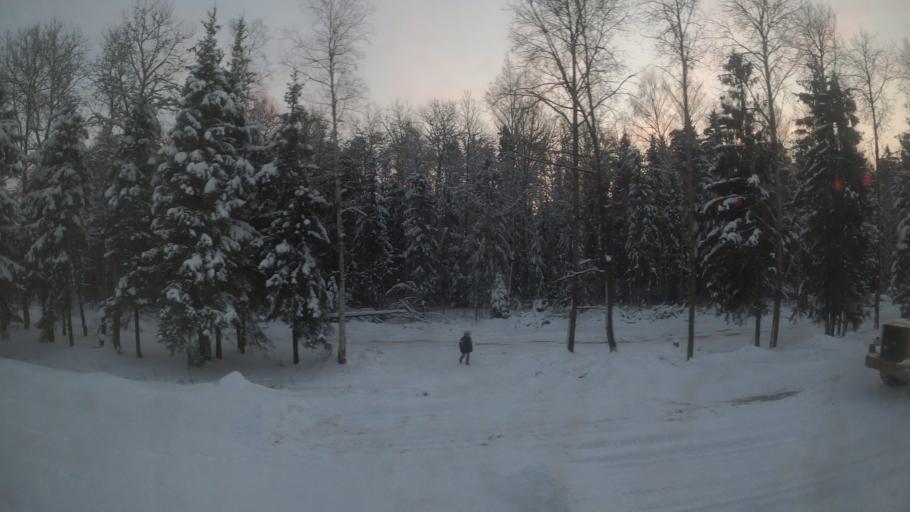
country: RU
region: Moskovskaya
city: Lugovaya
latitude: 56.0356
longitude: 37.4891
